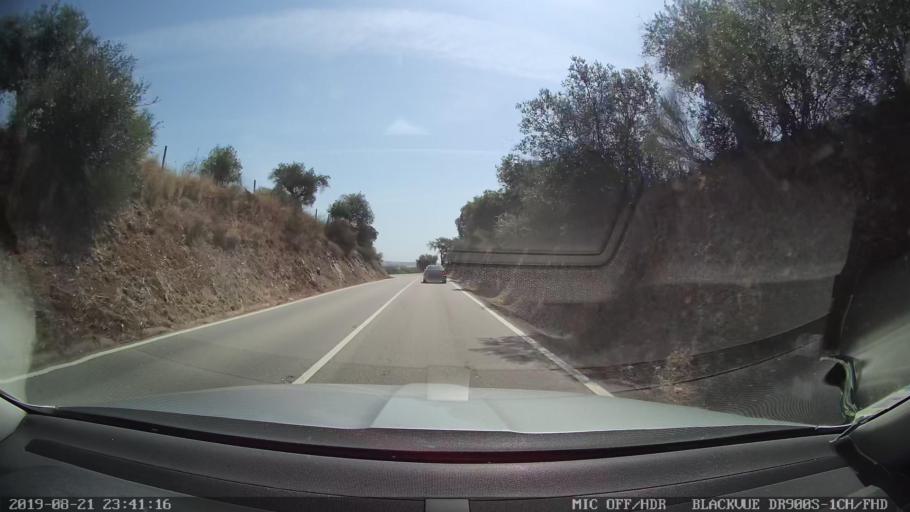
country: PT
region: Castelo Branco
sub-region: Idanha-A-Nova
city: Idanha-a-Nova
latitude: 39.8638
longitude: -7.3243
